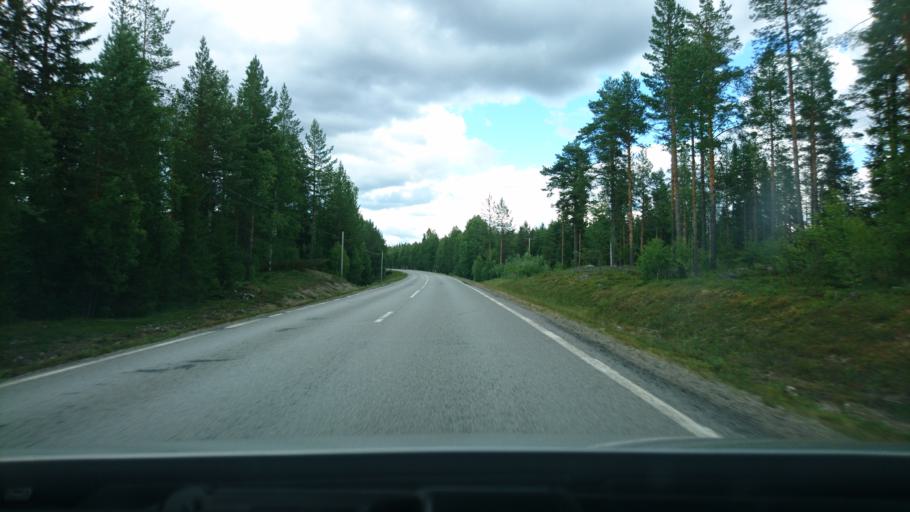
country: SE
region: Vaesterbotten
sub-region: Asele Kommun
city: Asele
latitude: 63.8724
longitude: 17.1947
